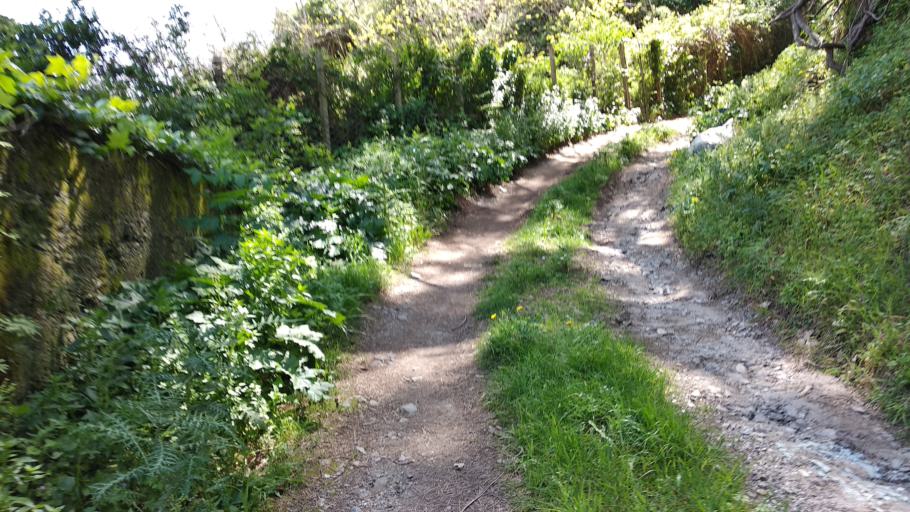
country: IT
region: Sicily
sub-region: Messina
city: Messina
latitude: 38.2128
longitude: 15.5142
